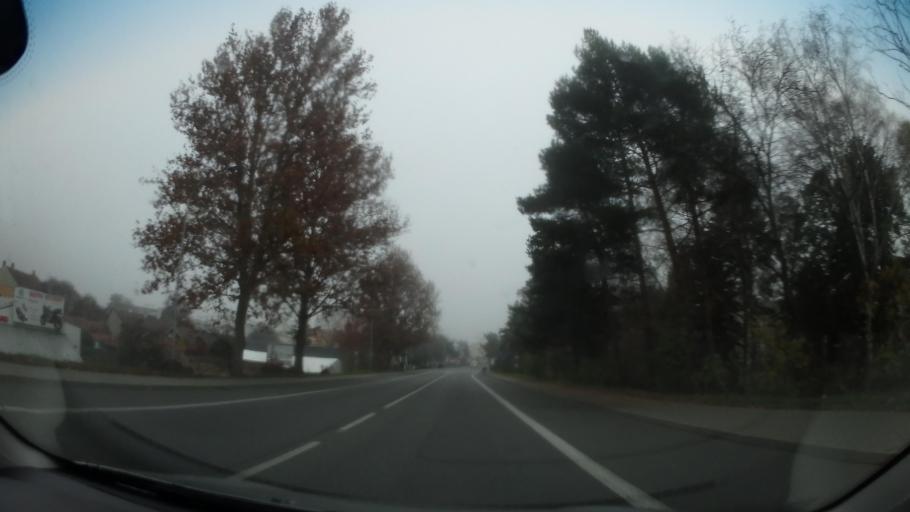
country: CZ
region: South Moravian
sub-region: Okres Hodonin
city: Kyjov
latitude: 49.0076
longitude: 17.1185
